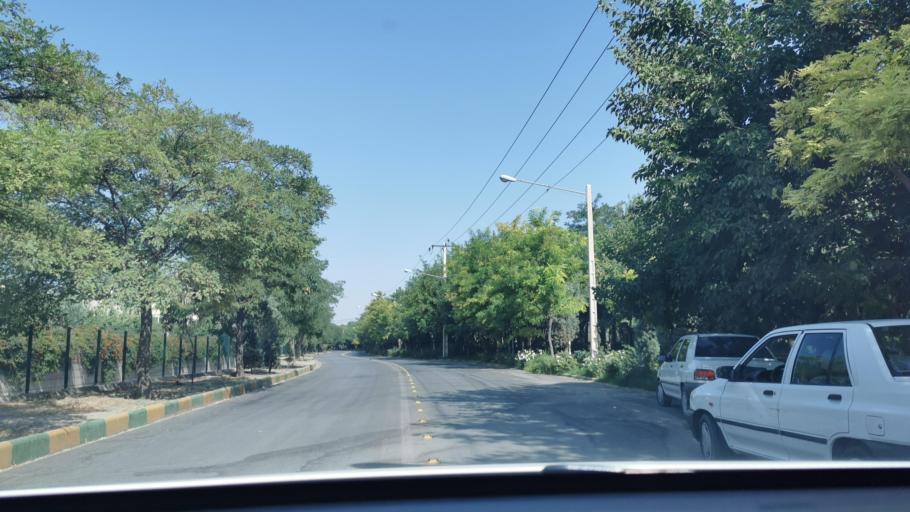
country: IR
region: Razavi Khorasan
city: Mashhad
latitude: 36.3291
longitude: 59.6368
